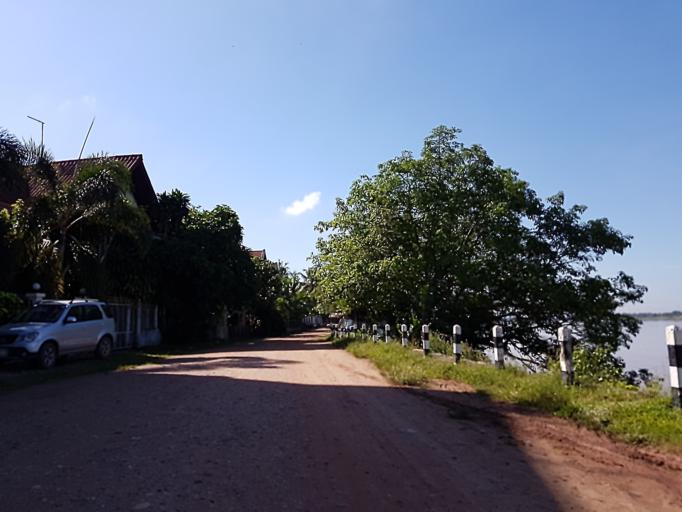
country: TH
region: Nong Khai
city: Si Chiang Mai
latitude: 17.9225
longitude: 102.6161
